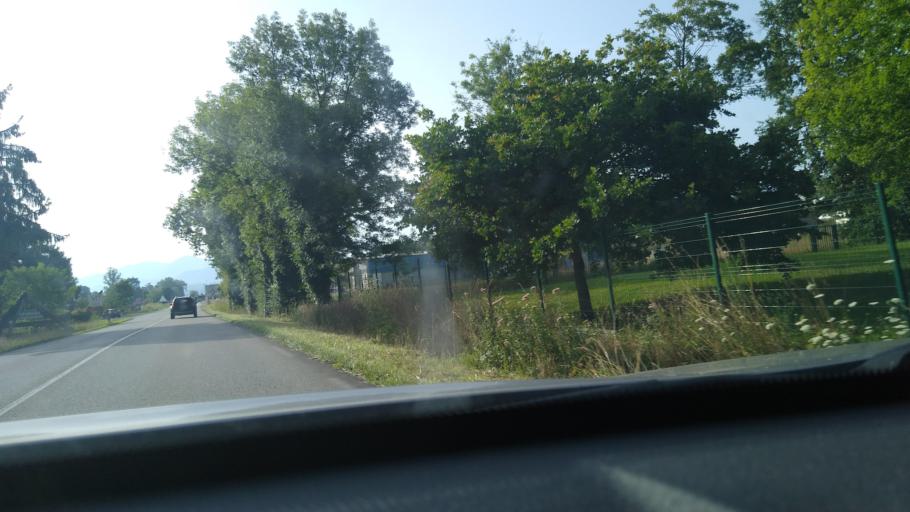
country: FR
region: Midi-Pyrenees
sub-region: Departement de l'Ariege
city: Saint-Lizier
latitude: 43.0230
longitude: 1.0954
